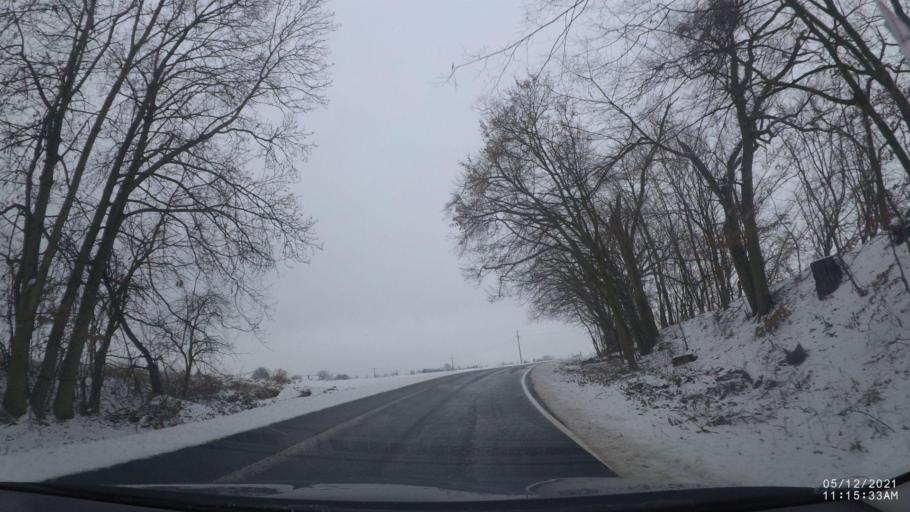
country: CZ
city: Solnice
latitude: 50.1844
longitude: 16.2182
